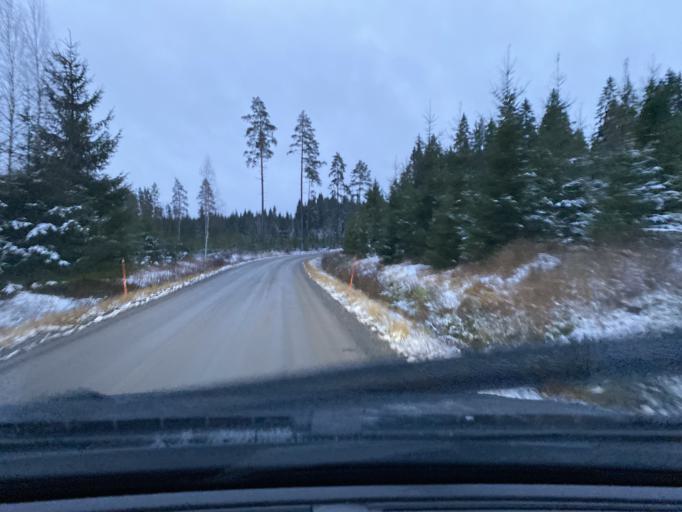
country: FI
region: Pirkanmaa
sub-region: Lounais-Pirkanmaa
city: Punkalaidun
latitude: 61.1582
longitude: 22.9461
